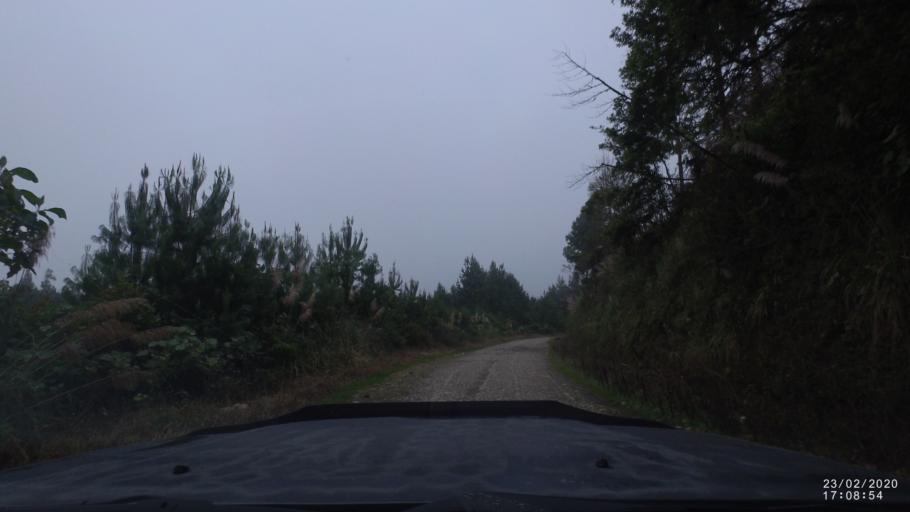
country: BO
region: Cochabamba
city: Colomi
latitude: -17.1306
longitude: -65.9542
